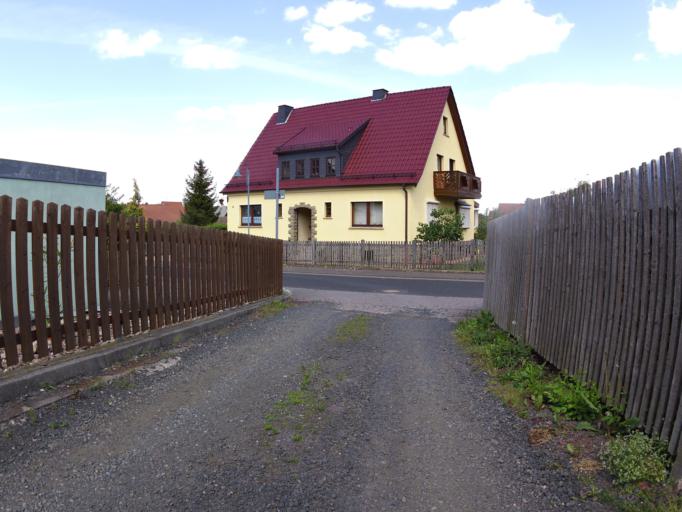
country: DE
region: Thuringia
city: Dermbach
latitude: 50.7125
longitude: 10.1187
